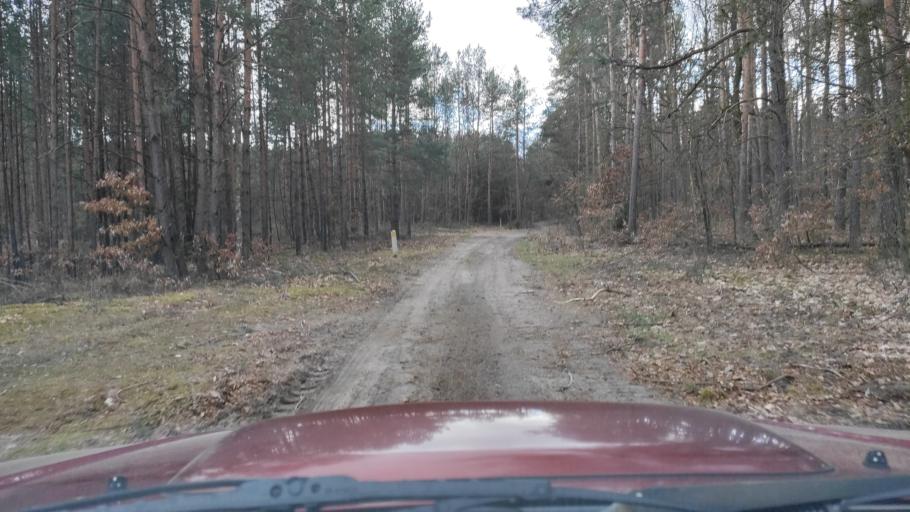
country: PL
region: Masovian Voivodeship
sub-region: Powiat kozienicki
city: Garbatka-Letnisko
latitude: 51.5112
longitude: 21.5635
